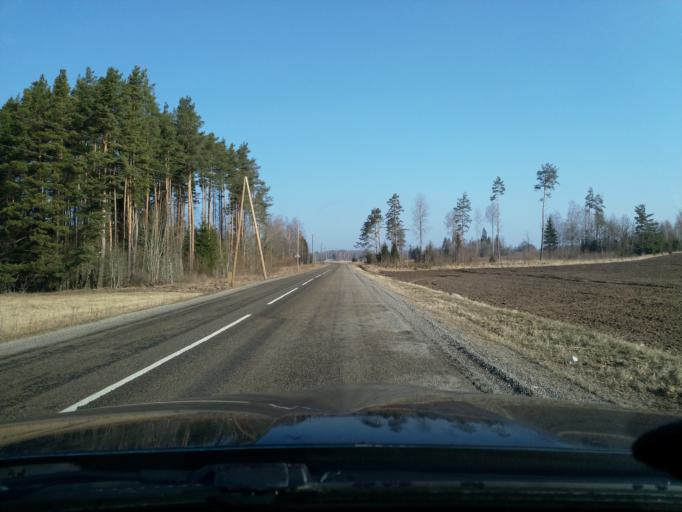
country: LV
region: Kuldigas Rajons
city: Kuldiga
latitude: 56.8714
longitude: 21.9396
